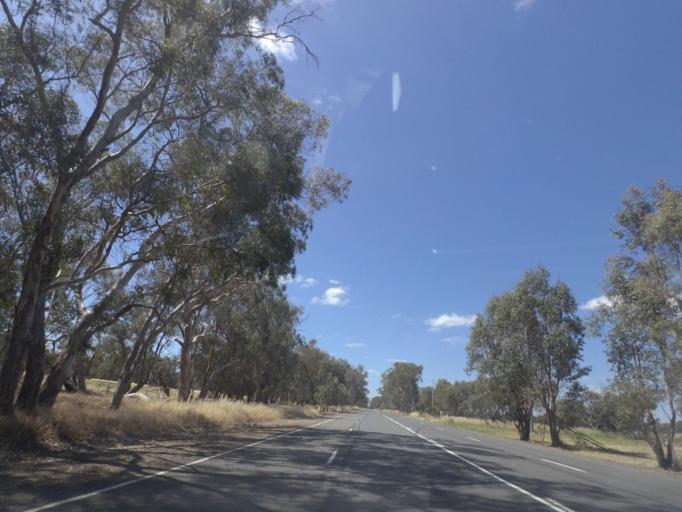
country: AU
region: Victoria
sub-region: Wangaratta
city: Wangaratta
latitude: -36.4267
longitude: 146.2568
